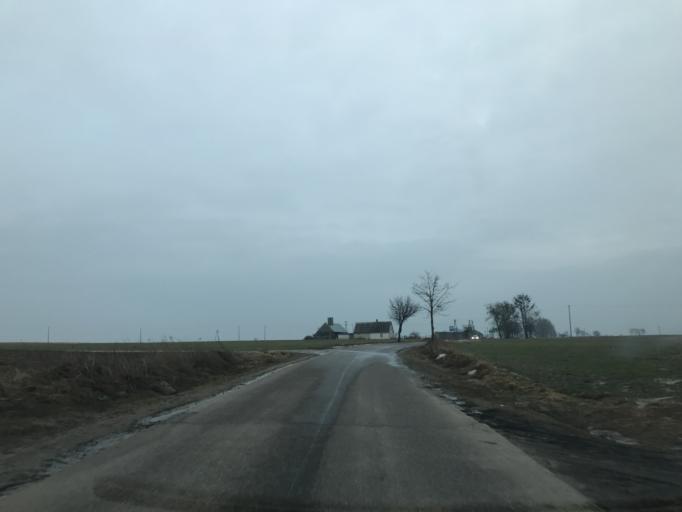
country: PL
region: Kujawsko-Pomorskie
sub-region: Powiat brodnicki
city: Bartniczka
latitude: 53.2378
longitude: 19.6003
